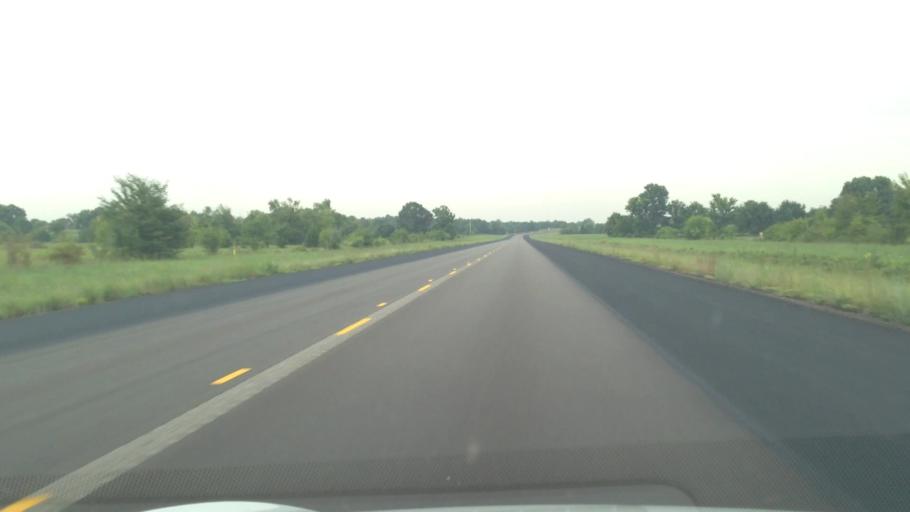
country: US
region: Kansas
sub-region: Cherokee County
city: Baxter Springs
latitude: 37.0342
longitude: -94.7063
